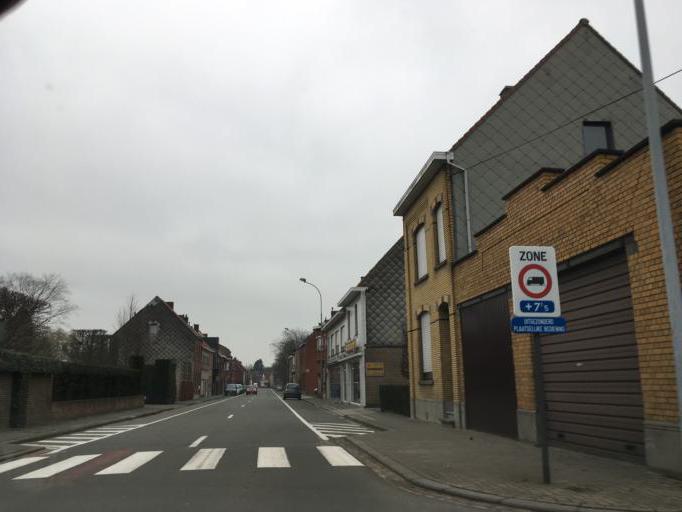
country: BE
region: Flanders
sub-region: Provincie West-Vlaanderen
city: Oostrozebeke
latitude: 50.9148
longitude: 3.3320
